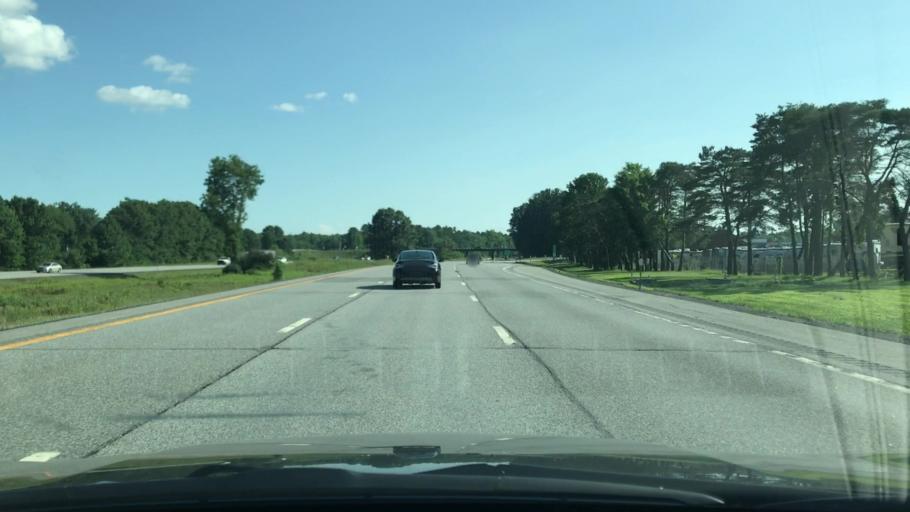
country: US
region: New York
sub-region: Saratoga County
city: Saratoga Springs
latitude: 43.1738
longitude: -73.7108
